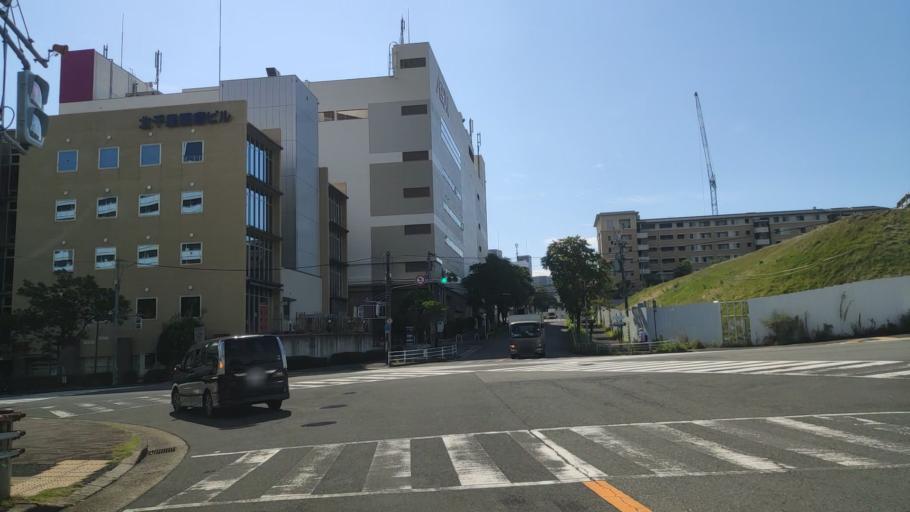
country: JP
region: Osaka
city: Mino
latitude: 34.8207
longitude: 135.5086
